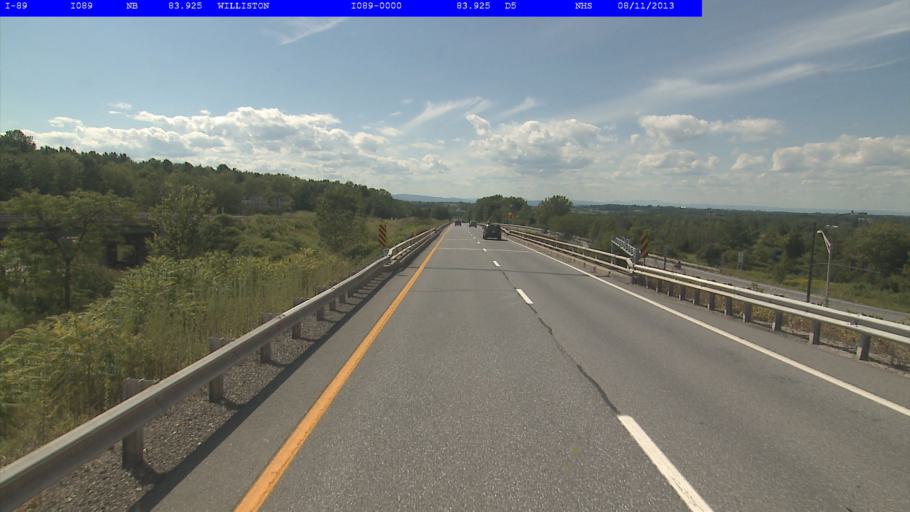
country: US
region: Vermont
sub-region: Chittenden County
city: Williston
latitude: 44.4394
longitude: -73.1142
